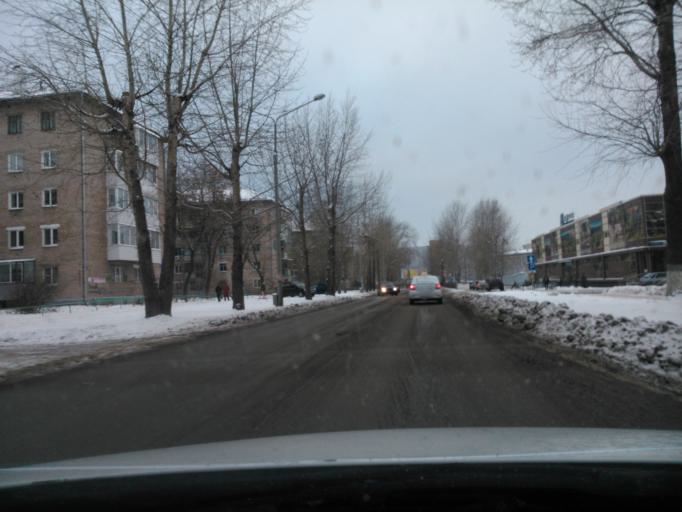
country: RU
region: Perm
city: Perm
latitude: 57.9879
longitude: 56.2050
